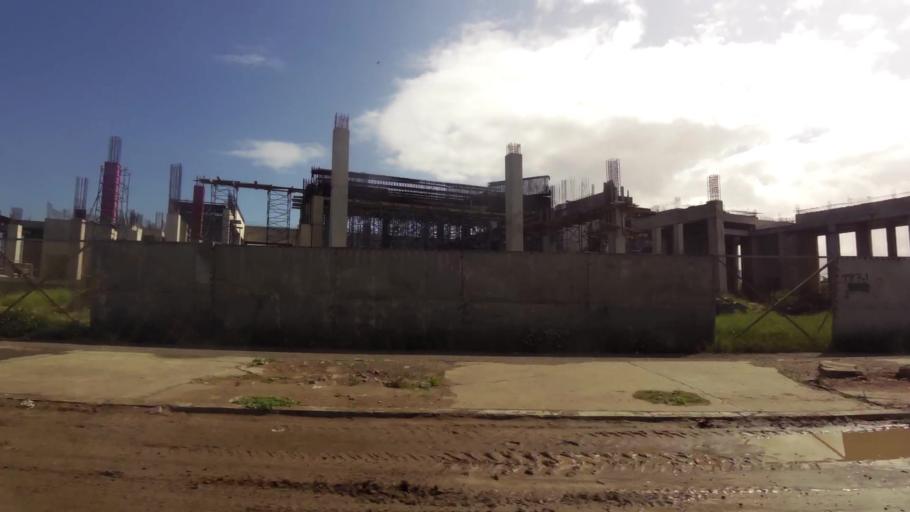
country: MA
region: Grand Casablanca
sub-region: Casablanca
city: Casablanca
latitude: 33.6043
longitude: -7.6193
